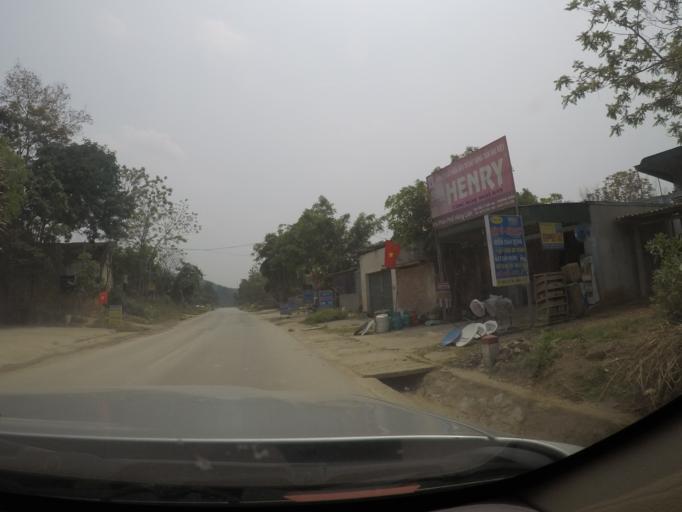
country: VN
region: Thanh Hoa
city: Thi Tran Thuong Xuan
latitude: 19.8000
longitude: 105.3968
